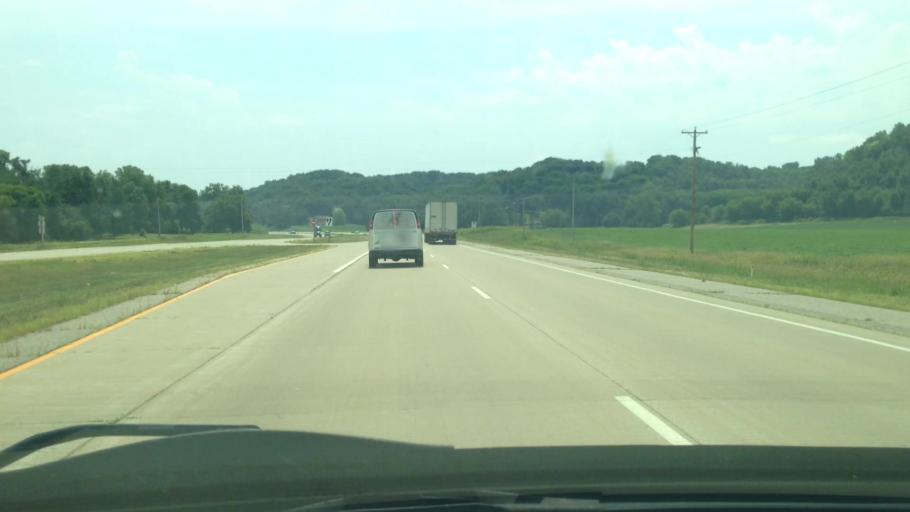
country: US
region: Wisconsin
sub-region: Sauk County
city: Sauk City
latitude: 43.2332
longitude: -89.6829
